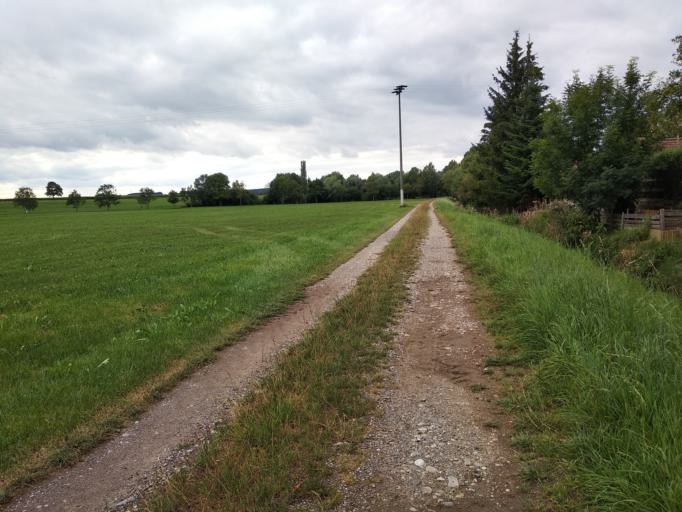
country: DE
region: Bavaria
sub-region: Swabia
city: Ungerhausen
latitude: 48.0096
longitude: 10.2699
